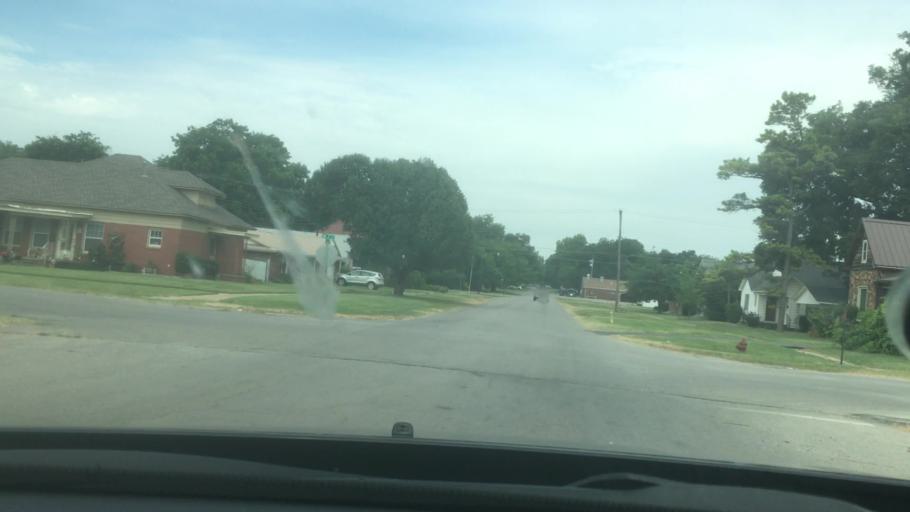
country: US
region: Oklahoma
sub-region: Garvin County
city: Lindsay
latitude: 34.8358
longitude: -97.6040
